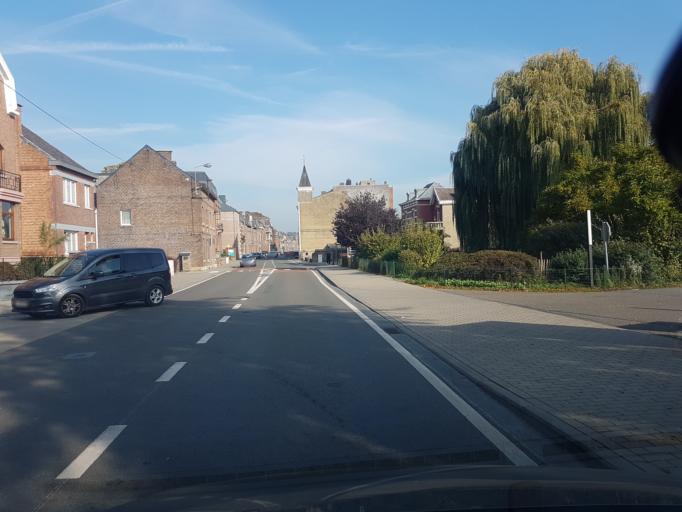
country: BE
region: Wallonia
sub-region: Province de Namur
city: Namur
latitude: 50.4518
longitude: 4.8688
